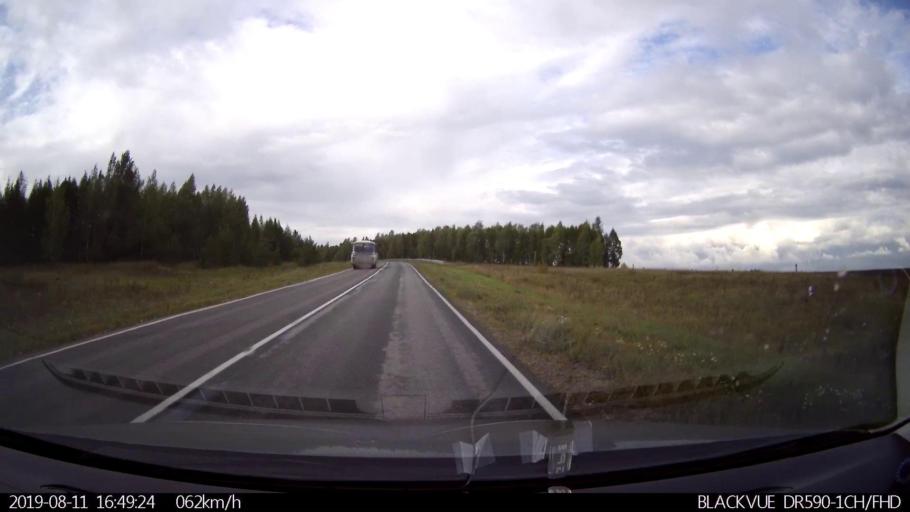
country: RU
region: Ulyanovsk
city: Mayna
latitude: 54.2203
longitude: 47.6957
